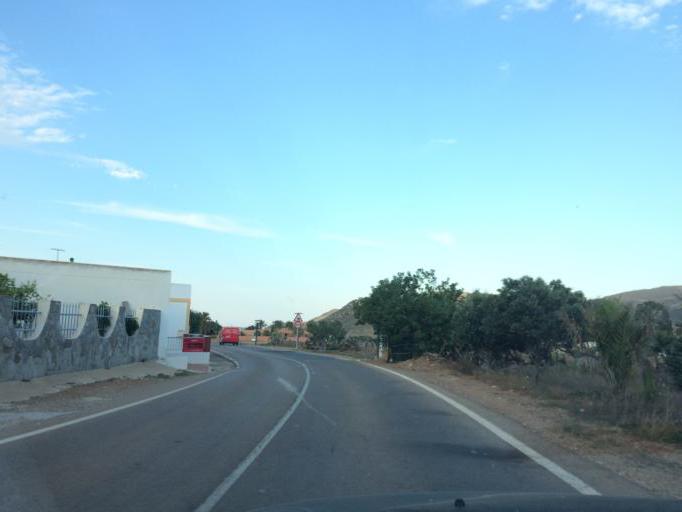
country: ES
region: Andalusia
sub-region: Provincia de Almeria
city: San Jose
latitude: 36.8494
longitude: -2.0339
